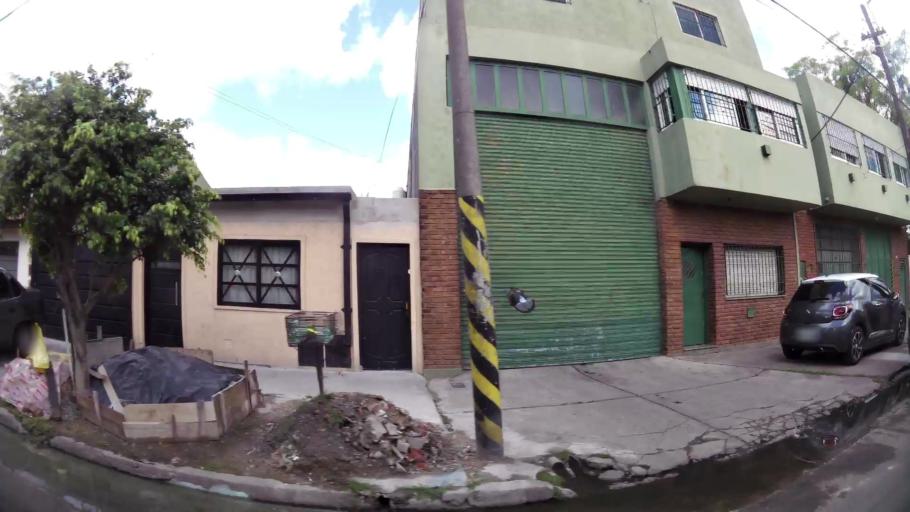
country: AR
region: Buenos Aires
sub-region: Partido de Lanus
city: Lanus
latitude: -34.6878
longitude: -58.4210
